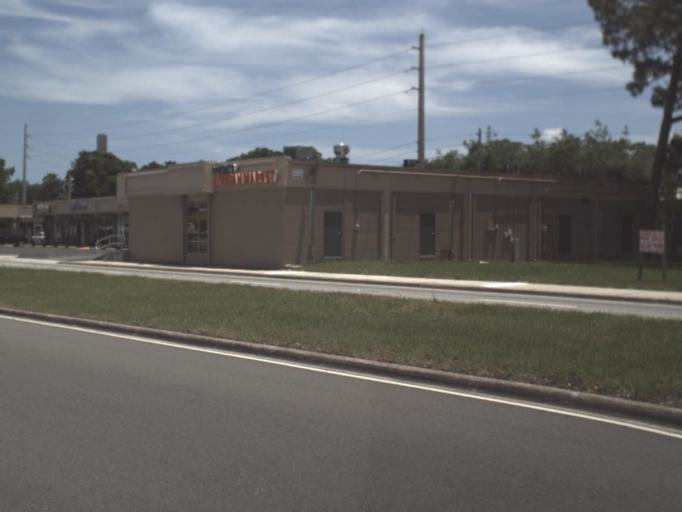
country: US
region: Florida
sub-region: Duval County
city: Jacksonville
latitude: 30.3274
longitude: -81.5879
